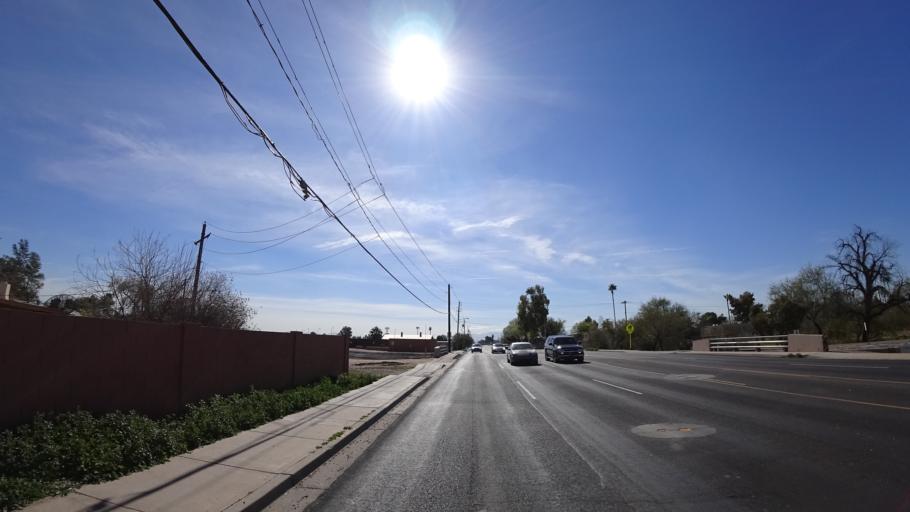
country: US
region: Arizona
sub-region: Maricopa County
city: Glendale
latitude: 33.4991
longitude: -112.2031
